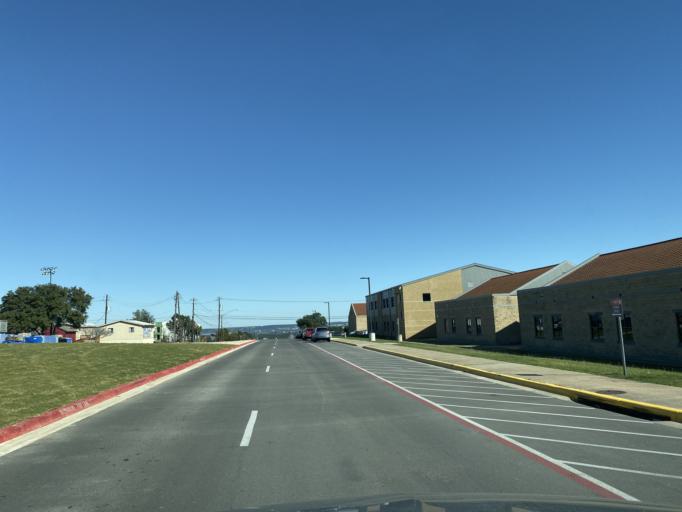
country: US
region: Texas
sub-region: Travis County
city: The Hills
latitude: 30.3278
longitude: -97.9704
